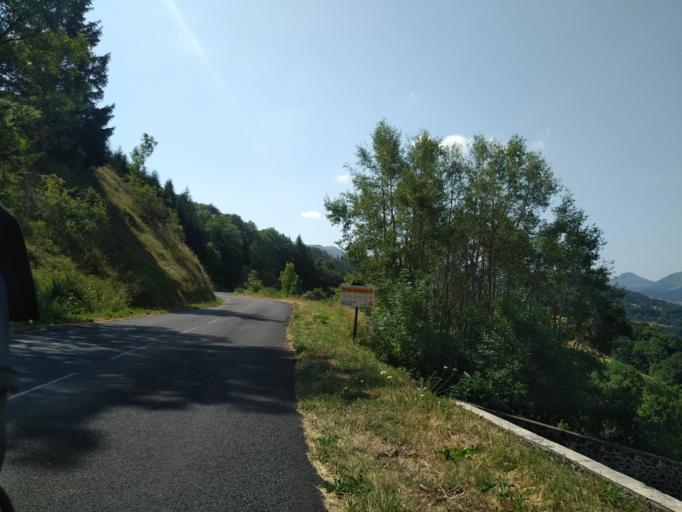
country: FR
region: Auvergne
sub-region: Departement du Cantal
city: Riom-es-Montagnes
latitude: 45.2031
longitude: 2.7161
